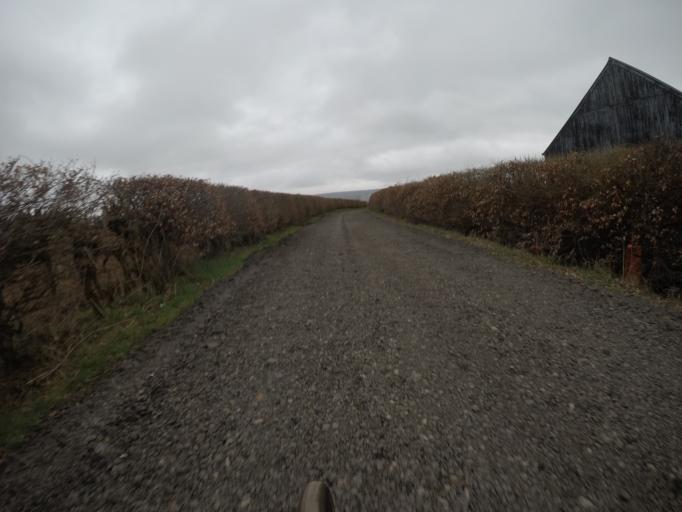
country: GB
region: Scotland
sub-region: East Ayrshire
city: Newmilns
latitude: 55.6232
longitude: -4.3432
